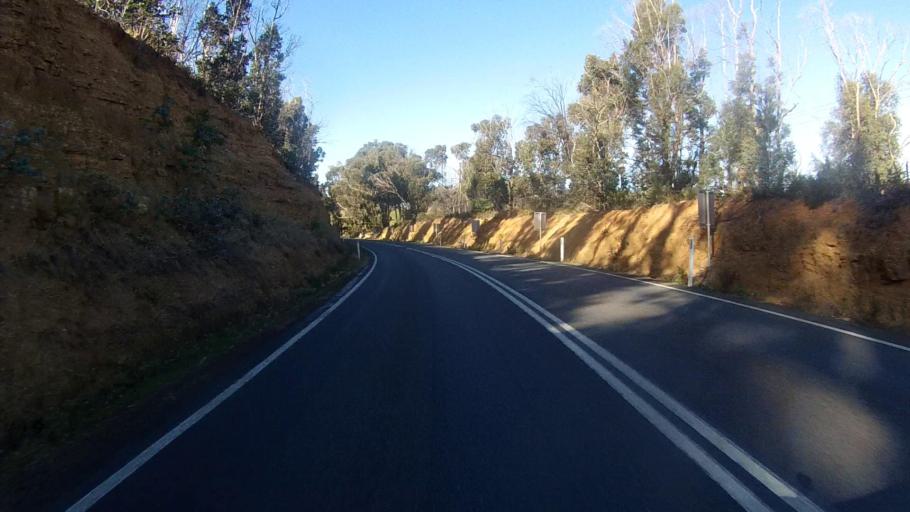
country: AU
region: Tasmania
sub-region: Sorell
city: Sorell
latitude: -42.8361
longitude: 147.8062
